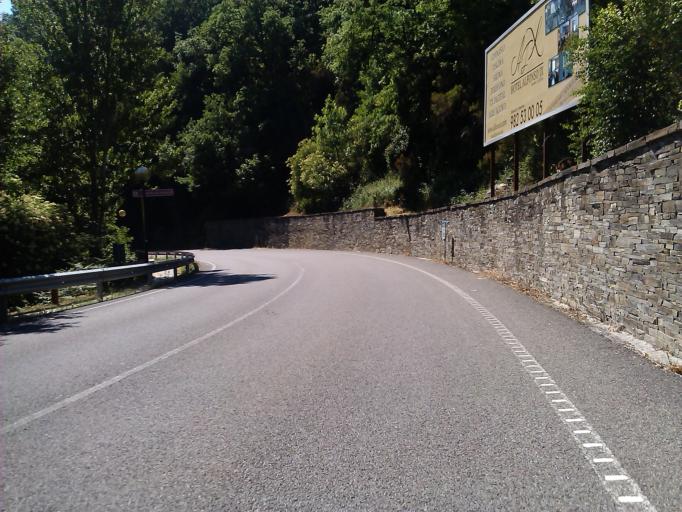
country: ES
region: Galicia
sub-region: Provincia de Lugo
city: Samos
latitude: 42.7307
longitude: -7.3325
